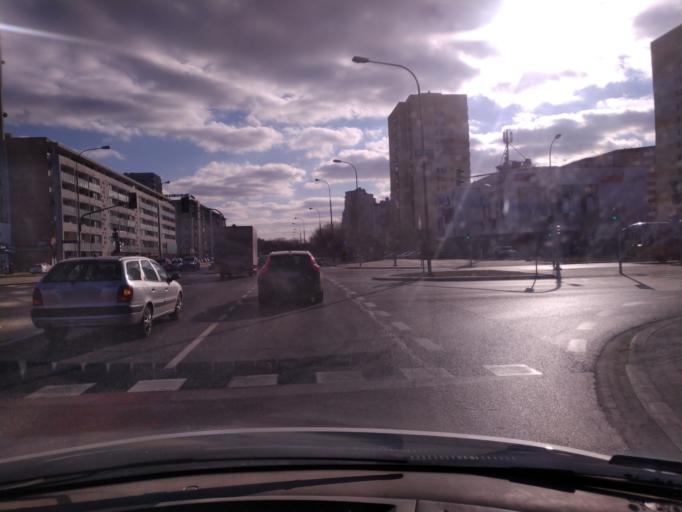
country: PL
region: Masovian Voivodeship
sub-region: Warszawa
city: Praga Poludnie
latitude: 52.2252
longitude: 21.0925
